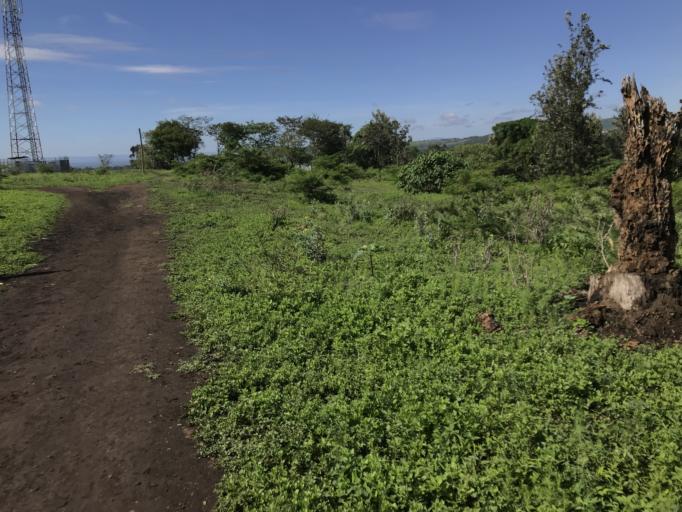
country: TZ
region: Arusha
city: Usa River
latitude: -3.3921
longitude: 36.7973
